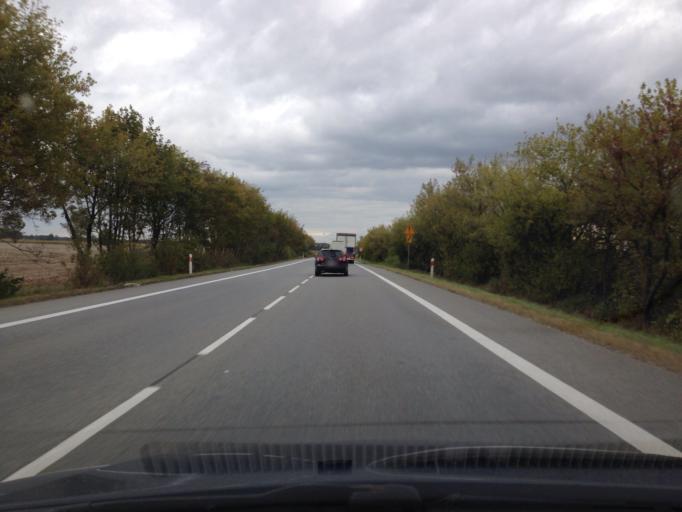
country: PL
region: Kujawsko-Pomorskie
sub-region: Powiat lipnowski
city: Skepe
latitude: 52.8638
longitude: 19.3125
